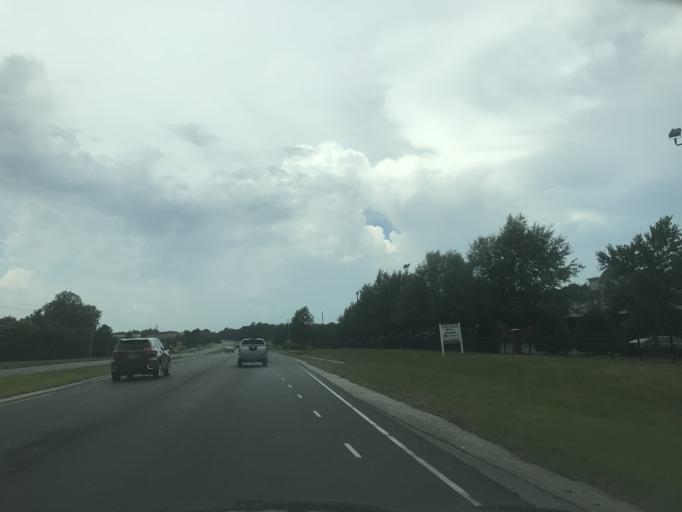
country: US
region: North Carolina
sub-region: Johnston County
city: Clayton
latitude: 35.6271
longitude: -78.4287
